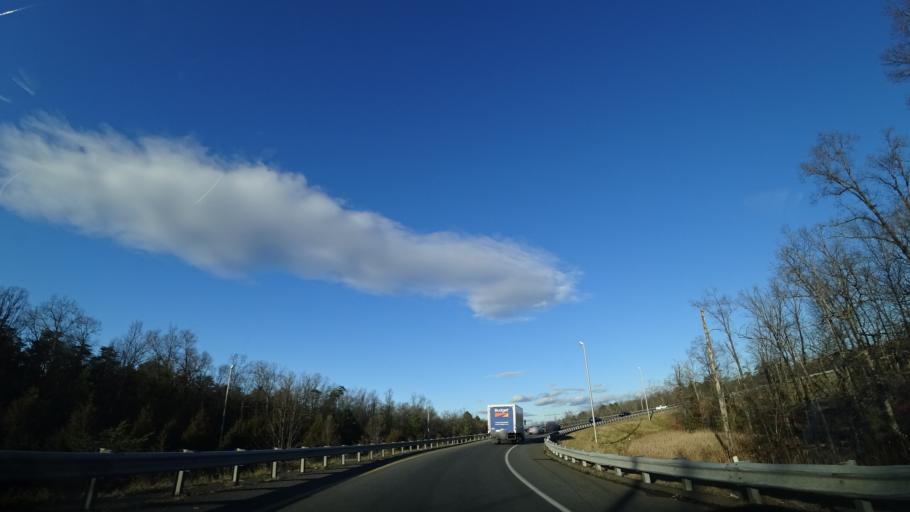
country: US
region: Virginia
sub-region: Prince William County
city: Gainesville
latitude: 38.7991
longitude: -77.5763
